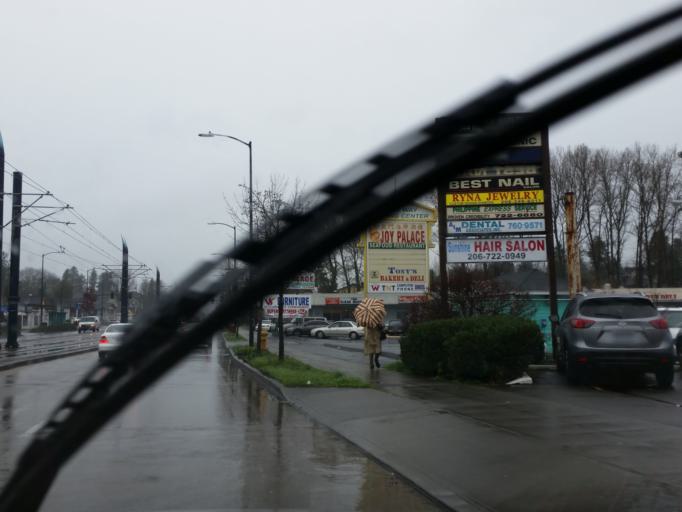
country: US
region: Washington
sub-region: King County
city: Riverton
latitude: 47.5468
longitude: -122.2858
